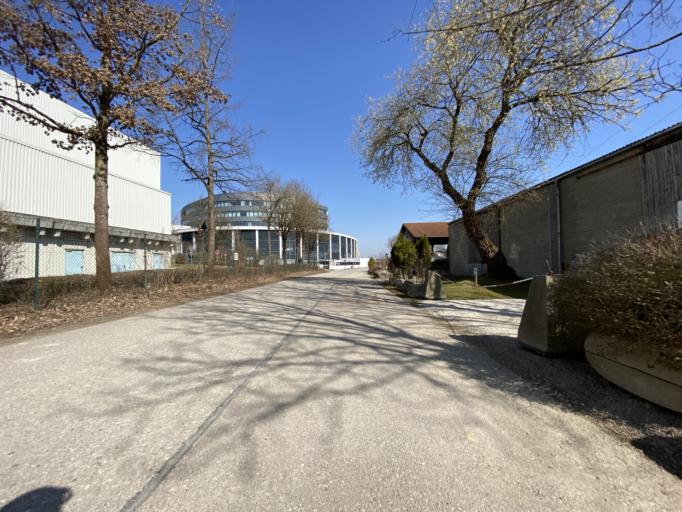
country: DE
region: Bavaria
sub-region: Upper Bavaria
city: Unterfoehring
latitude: 48.1899
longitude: 11.6578
